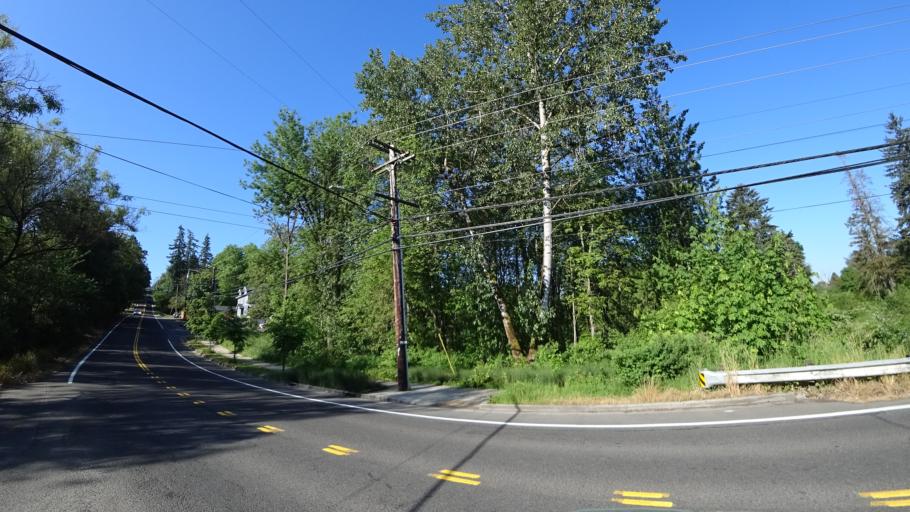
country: US
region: Oregon
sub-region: Multnomah County
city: Lents
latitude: 45.4738
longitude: -122.5481
